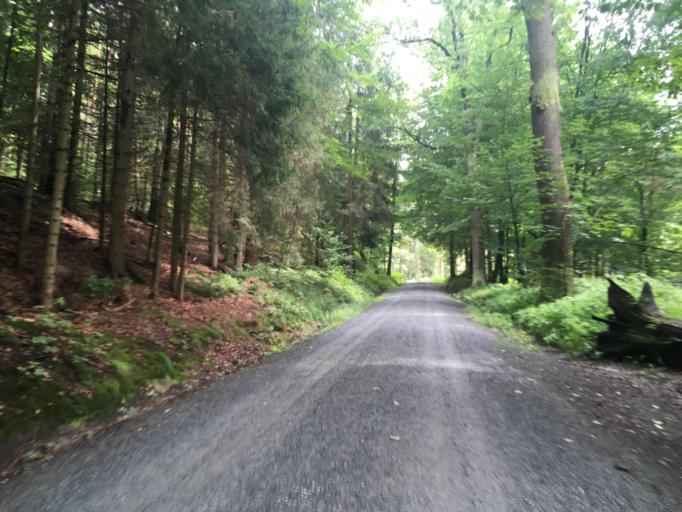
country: DE
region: Saxony
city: Bad Schandau
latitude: 50.9190
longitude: 14.2020
